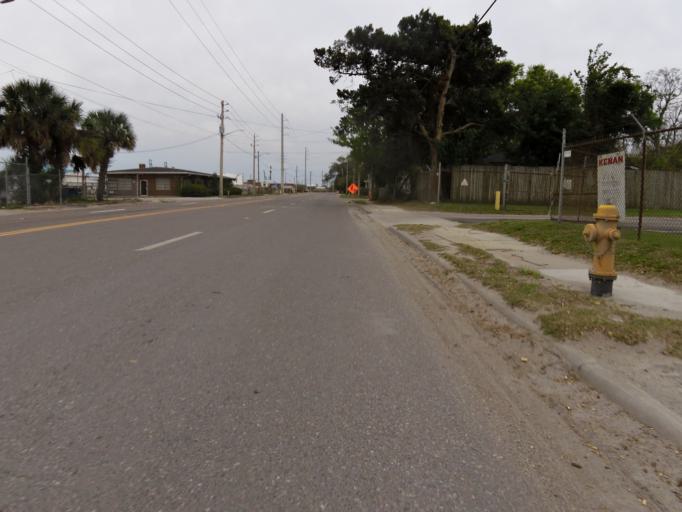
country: US
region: Florida
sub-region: Duval County
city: Jacksonville
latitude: 30.3618
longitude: -81.6274
